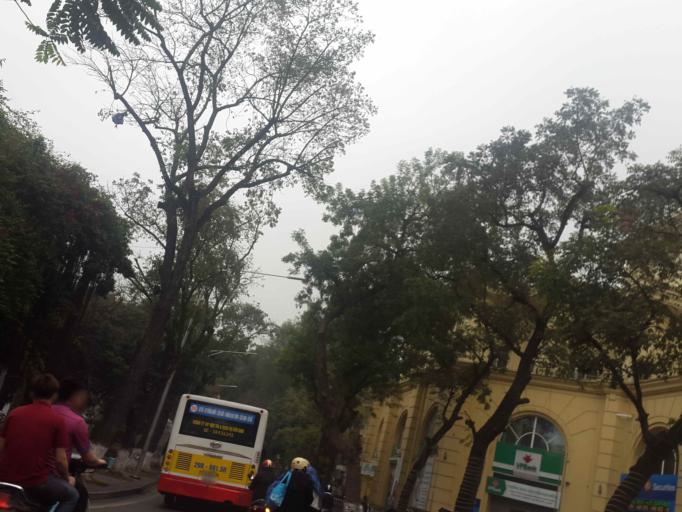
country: VN
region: Ha Noi
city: Hoan Kiem
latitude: 21.0312
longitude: 105.8509
